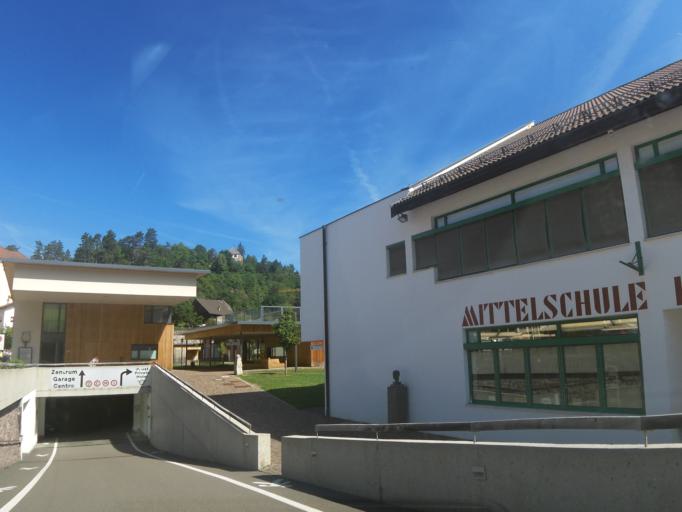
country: IT
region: Trentino-Alto Adige
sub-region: Bolzano
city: Castelrotto
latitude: 46.5676
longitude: 11.5617
